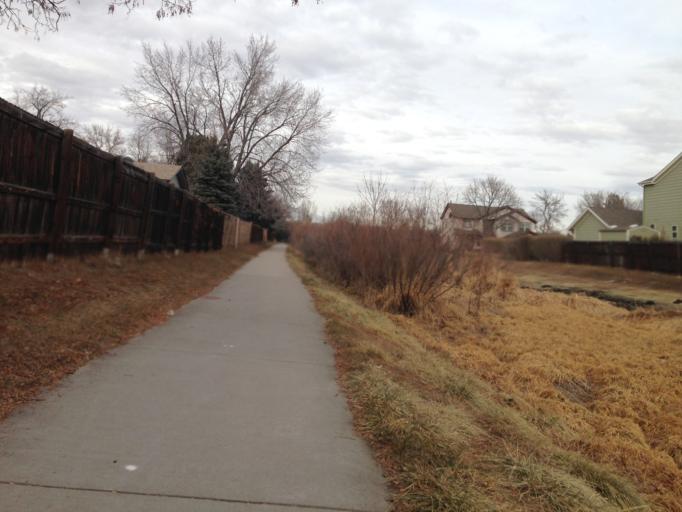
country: US
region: Colorado
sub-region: Adams County
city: Westminster
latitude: 39.8458
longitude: -105.0629
